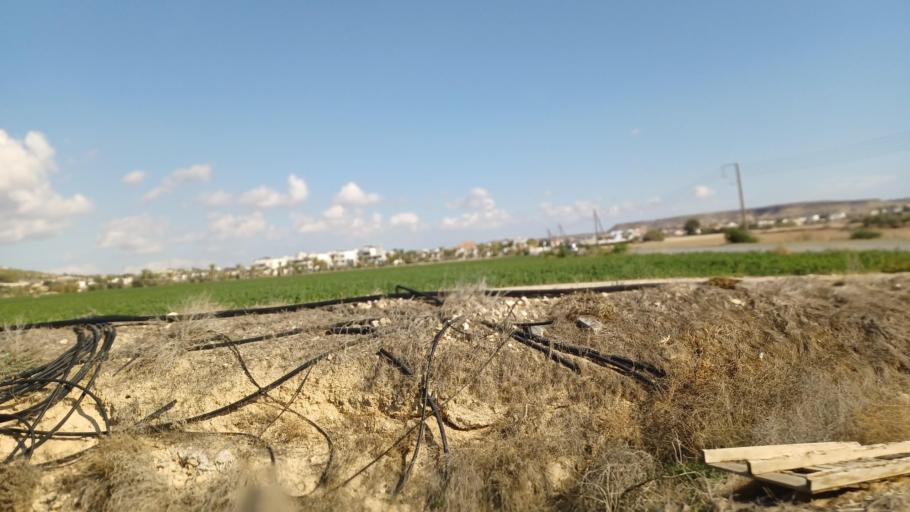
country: CY
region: Larnaka
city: Voroklini
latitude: 34.9929
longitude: 33.6700
